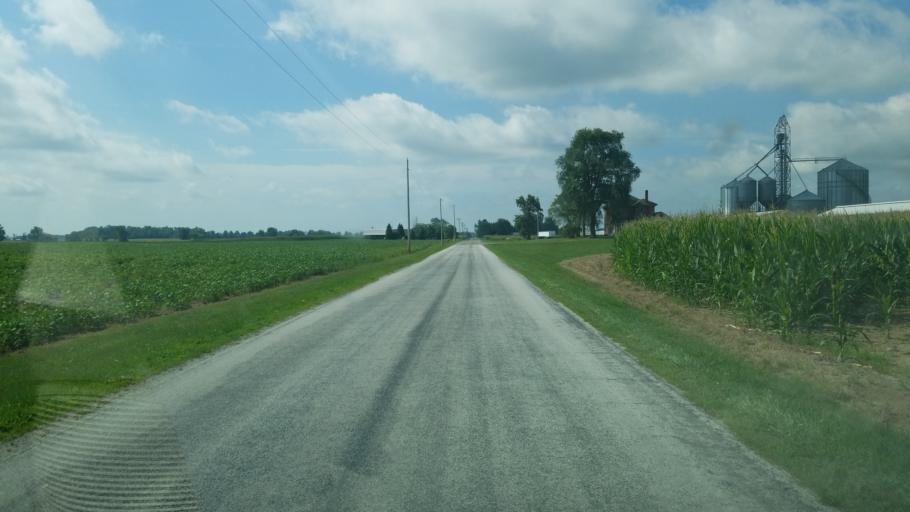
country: US
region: Ohio
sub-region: Hardin County
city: Kenton
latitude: 40.6008
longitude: -83.4443
